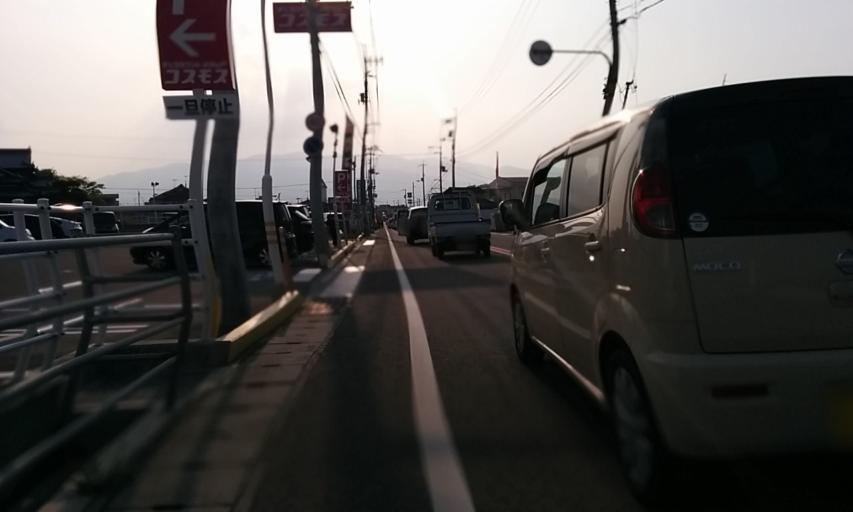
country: JP
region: Ehime
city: Saijo
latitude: 33.8963
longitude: 133.1230
